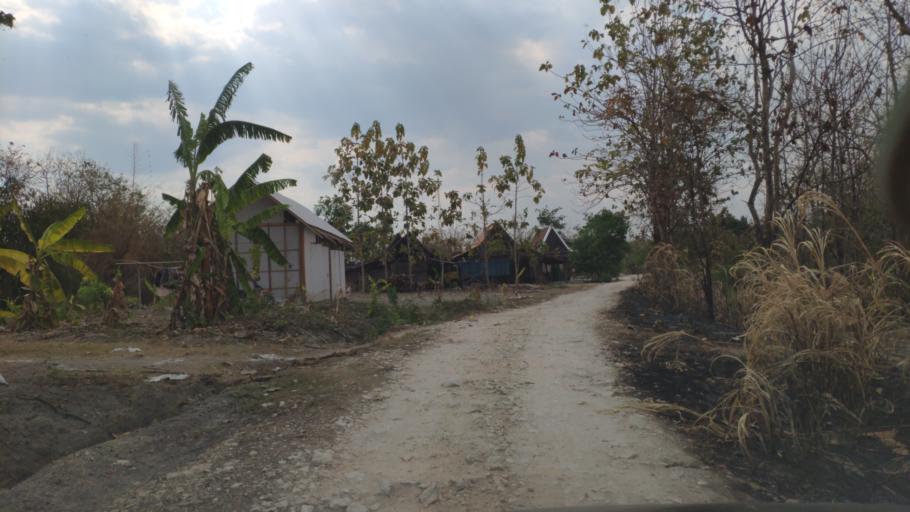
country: ID
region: Central Java
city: Randublatung
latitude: -7.3029
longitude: 111.3390
